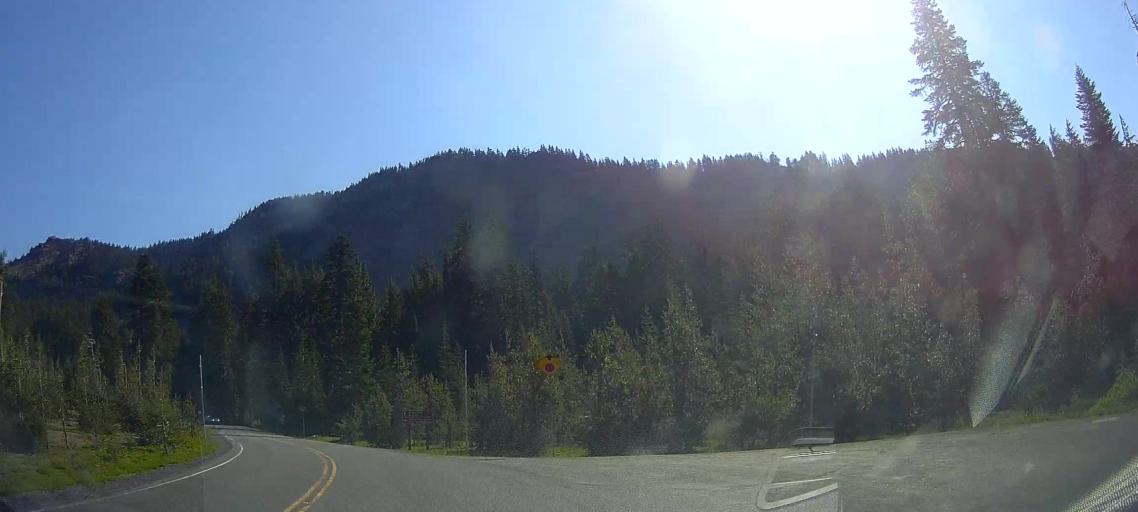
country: US
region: Oregon
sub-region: Jackson County
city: Shady Cove
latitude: 42.8955
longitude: -122.1344
